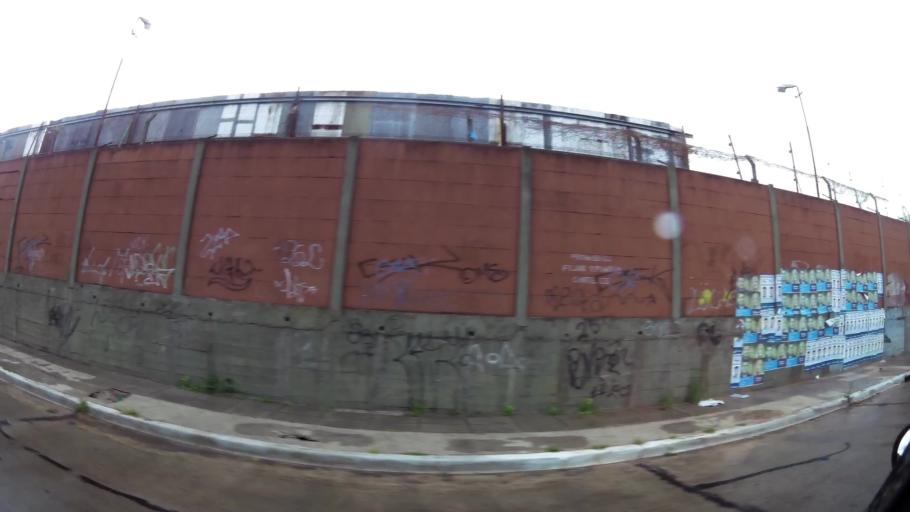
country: AR
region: Buenos Aires
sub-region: Partido de Quilmes
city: Quilmes
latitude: -34.7681
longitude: -58.2086
